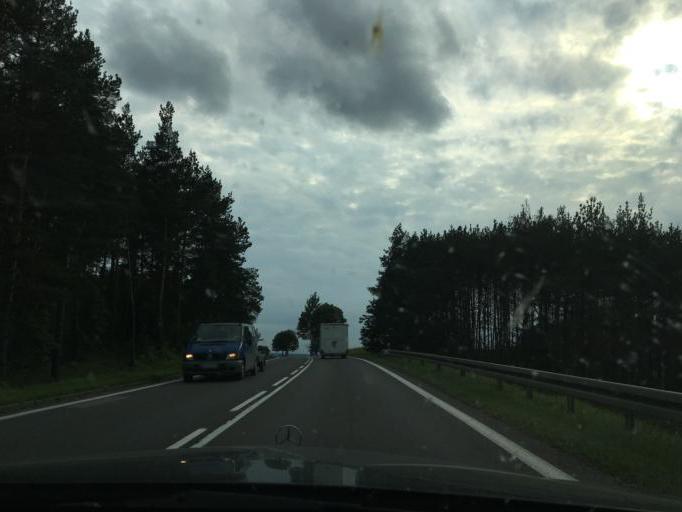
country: PL
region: Podlasie
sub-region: Powiat kolnenski
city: Stawiski
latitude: 53.4370
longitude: 22.1745
